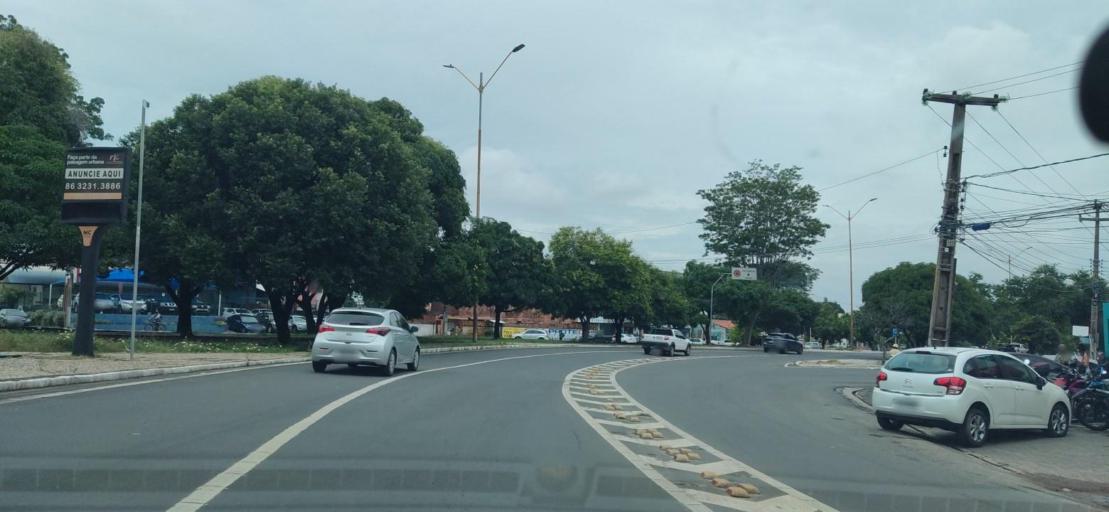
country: BR
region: Piaui
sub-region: Teresina
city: Teresina
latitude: -5.0809
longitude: -42.7753
